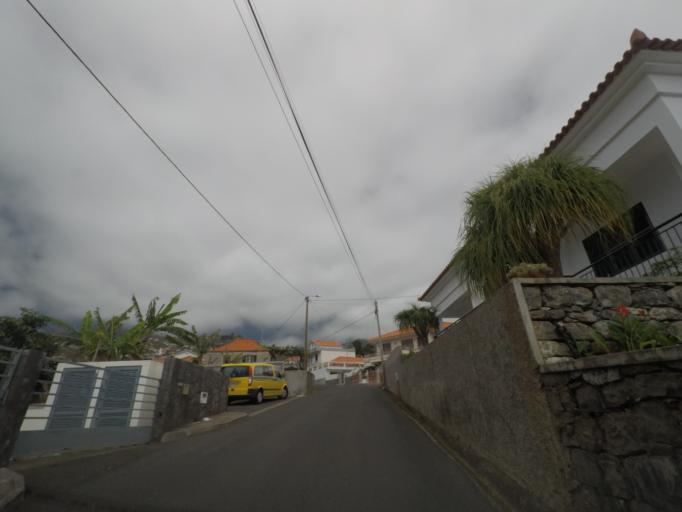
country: PT
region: Madeira
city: Ponta do Sol
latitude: 32.6872
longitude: -17.1016
